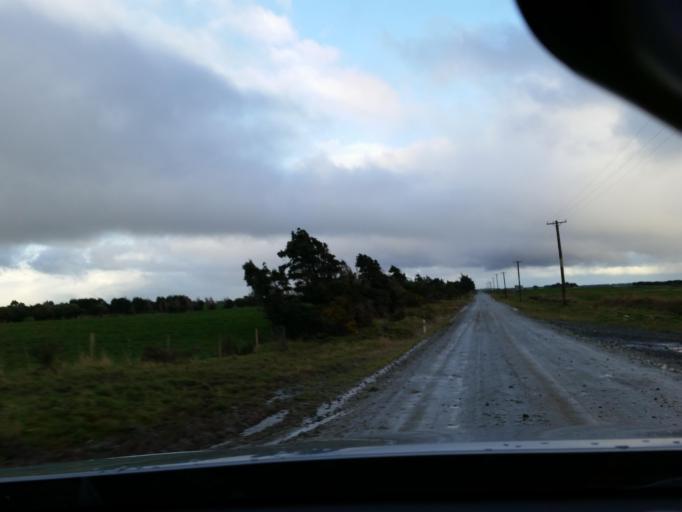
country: NZ
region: Southland
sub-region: Invercargill City
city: Invercargill
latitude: -46.4250
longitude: 168.5061
